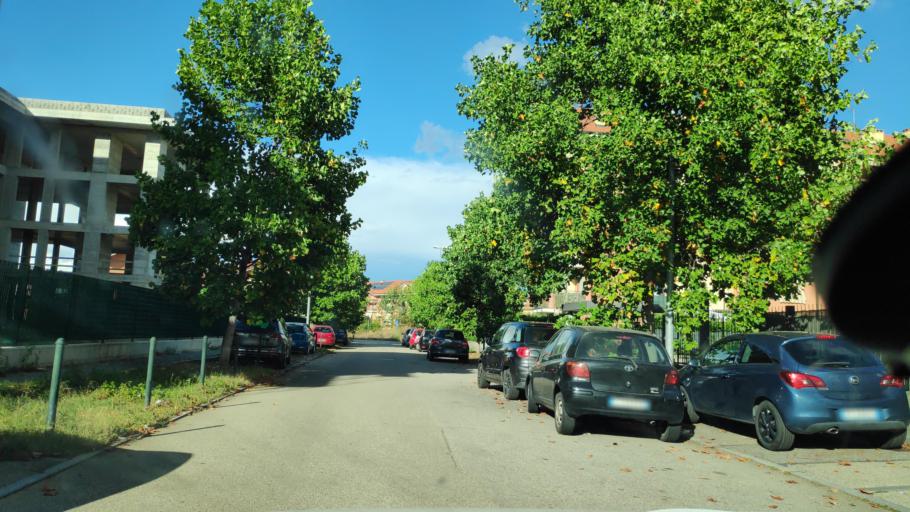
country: IT
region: Piedmont
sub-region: Provincia di Torino
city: La Loggia
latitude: 44.9531
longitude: 7.6734
